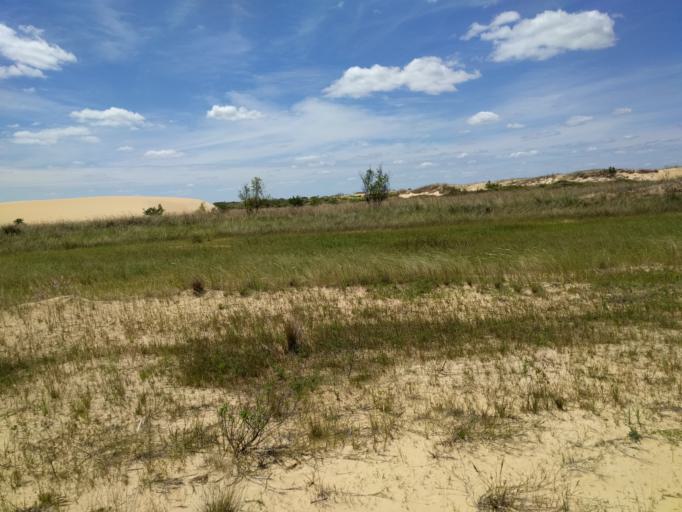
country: BO
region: Santa Cruz
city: Santa Cruz de la Sierra
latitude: -17.9508
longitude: -63.1519
